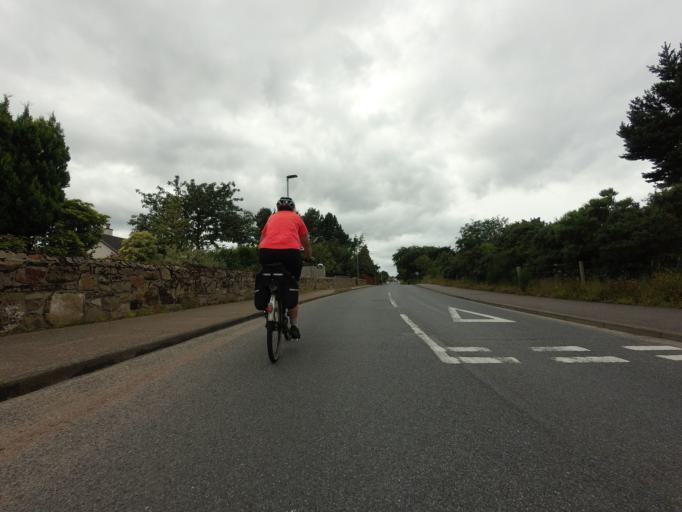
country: GB
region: Scotland
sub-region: Highland
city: Nairn
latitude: 57.5872
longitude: -3.8521
